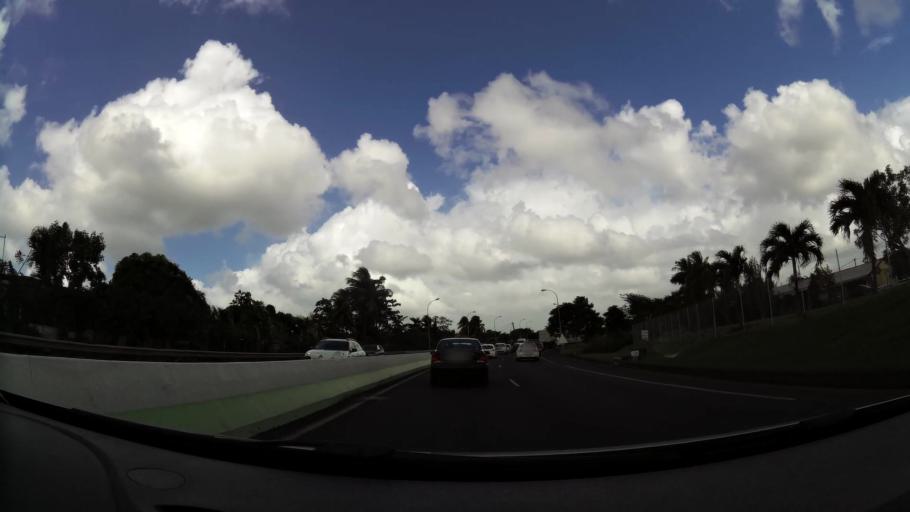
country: MQ
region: Martinique
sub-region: Martinique
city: Ducos
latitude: 14.5311
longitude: -60.9833
